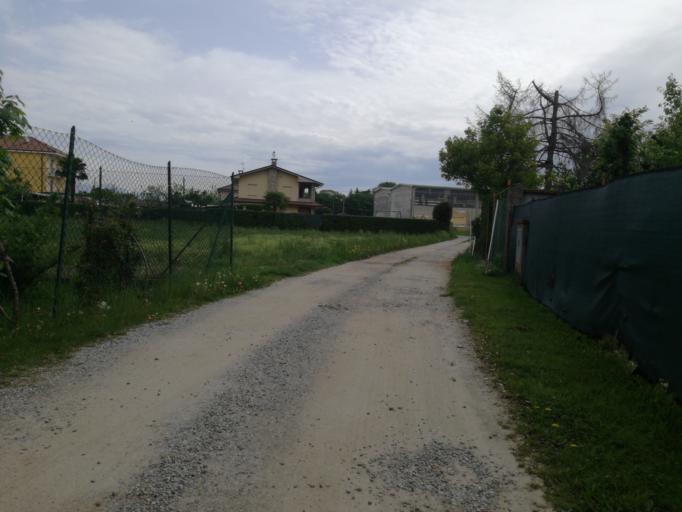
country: IT
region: Lombardy
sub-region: Provincia di Monza e Brianza
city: Porto d'Adda
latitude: 45.6499
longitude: 9.4574
